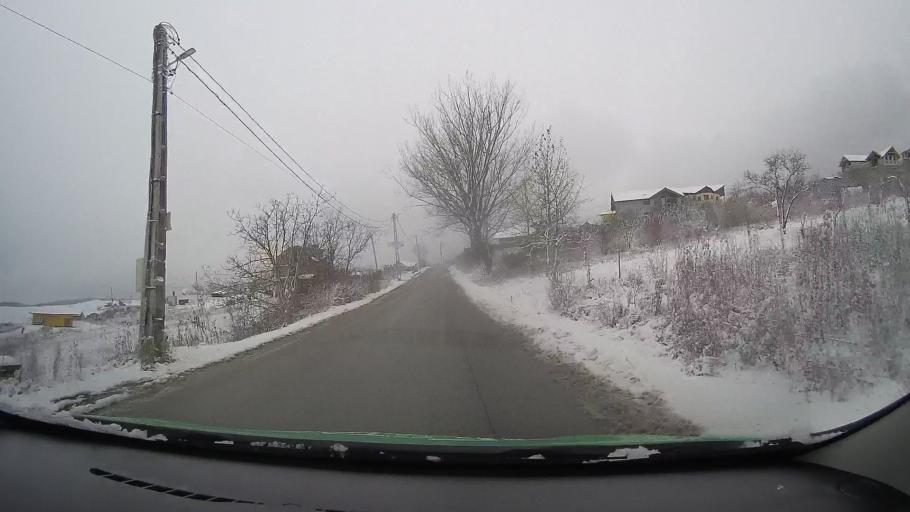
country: RO
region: Hunedoara
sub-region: Municipiul Deva
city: Deva
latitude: 45.8670
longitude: 22.8896
